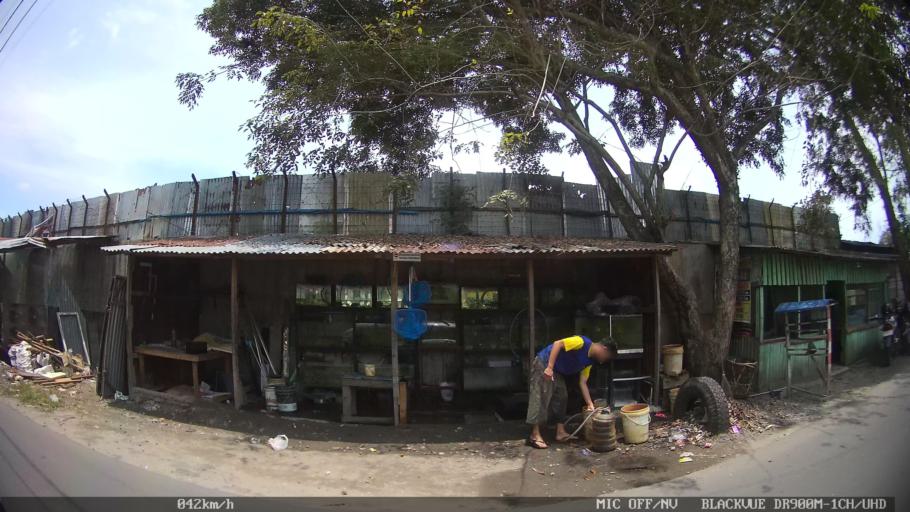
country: ID
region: North Sumatra
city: Labuhan Deli
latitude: 3.7091
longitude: 98.6723
